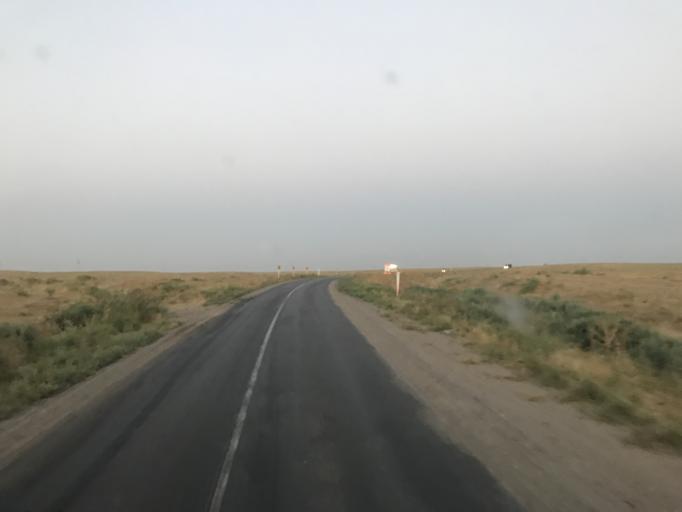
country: UZ
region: Toshkent
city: Chinoz
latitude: 41.1985
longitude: 68.6119
